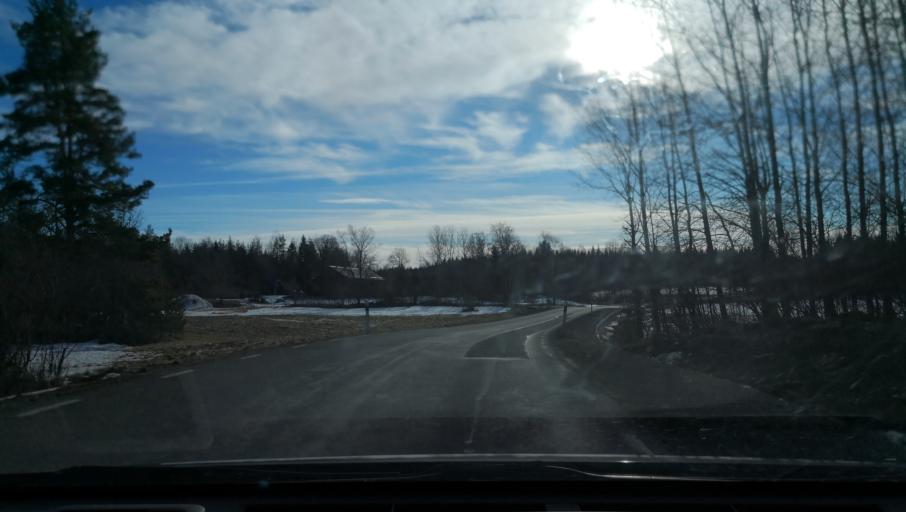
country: SE
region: Uppsala
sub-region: Osthammars Kommun
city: Osterbybruk
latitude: 60.2450
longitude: 17.9357
